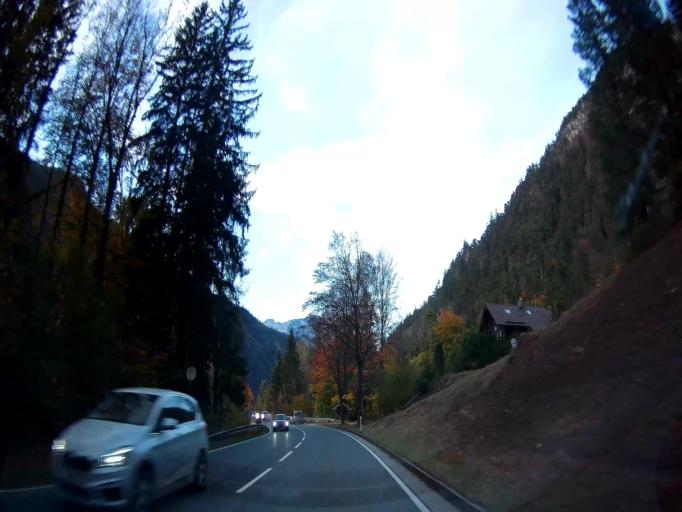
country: DE
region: Bavaria
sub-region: Upper Bavaria
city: Bad Reichenhall
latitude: 47.6919
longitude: 12.8498
